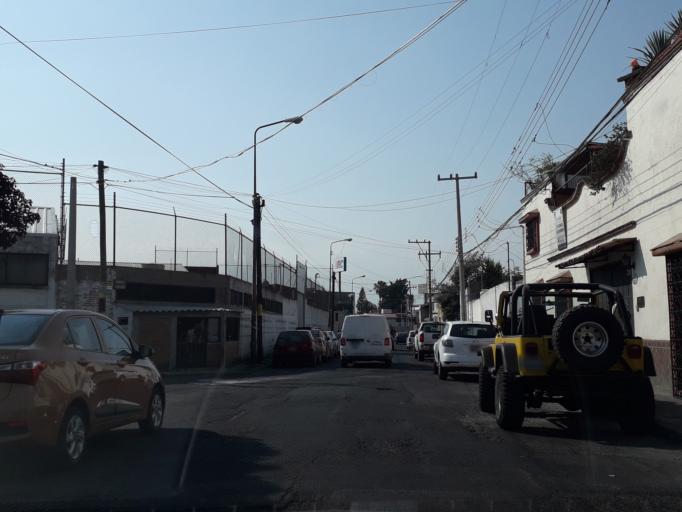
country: MX
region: Puebla
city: Puebla
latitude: 19.0152
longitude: -98.2136
